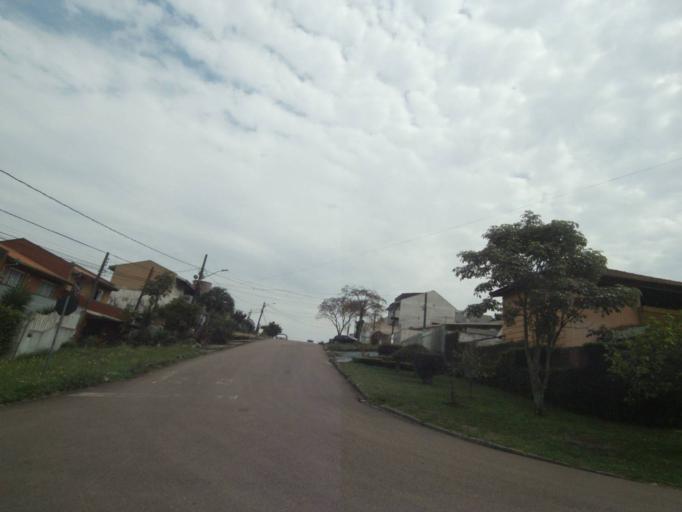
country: BR
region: Parana
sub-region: Pinhais
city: Pinhais
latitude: -25.4204
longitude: -49.2103
